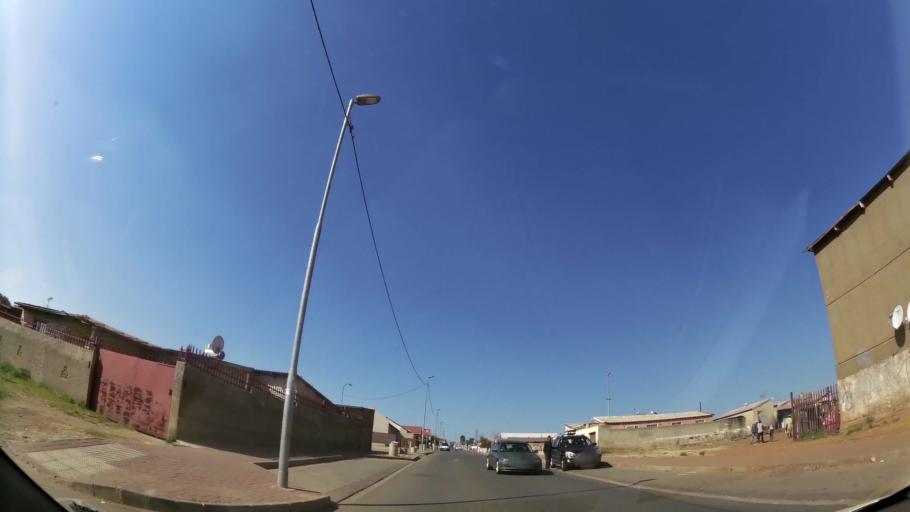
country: ZA
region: Gauteng
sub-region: City of Johannesburg Metropolitan Municipality
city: Johannesburg
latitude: -26.1834
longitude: 27.9720
